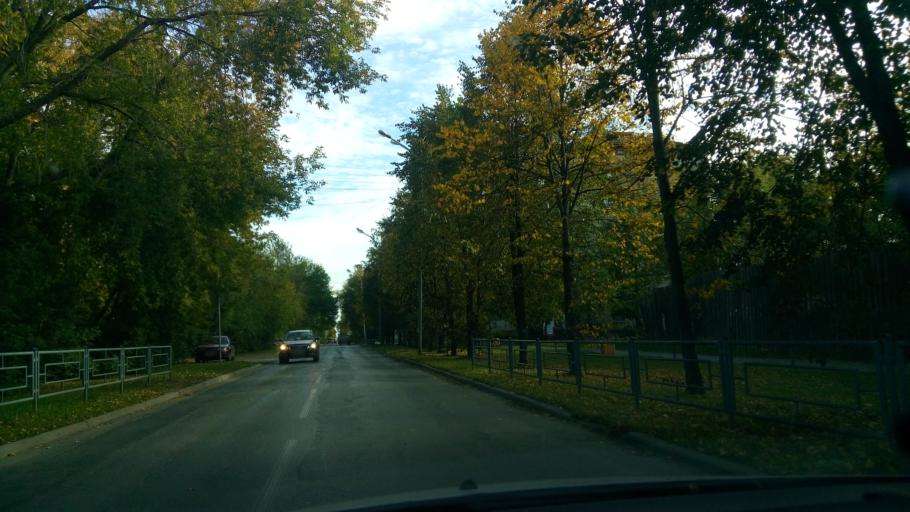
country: RU
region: Sverdlovsk
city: Yekaterinburg
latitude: 56.8914
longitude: 60.6190
